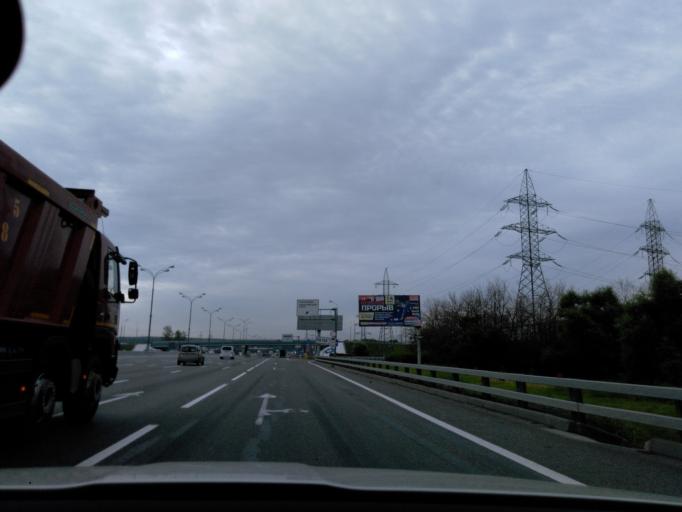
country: RU
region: Moscow
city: Gol'yanovo
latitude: 55.8314
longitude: 37.8247
